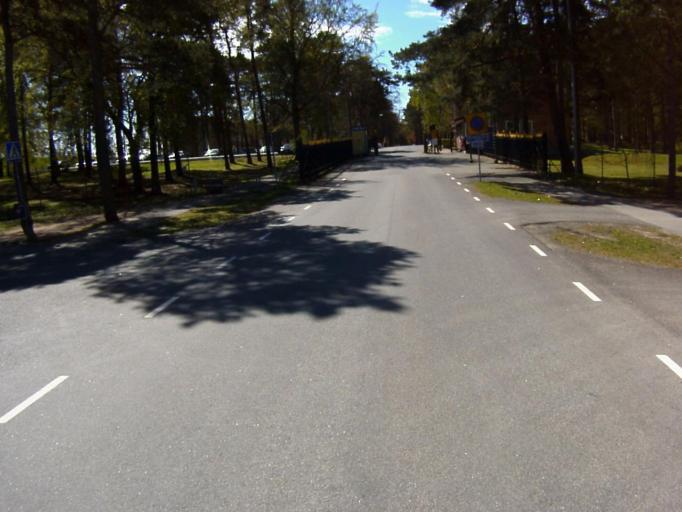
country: SE
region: Skane
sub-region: Kristianstads Kommun
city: Norra Asum
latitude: 55.9898
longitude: 14.1451
